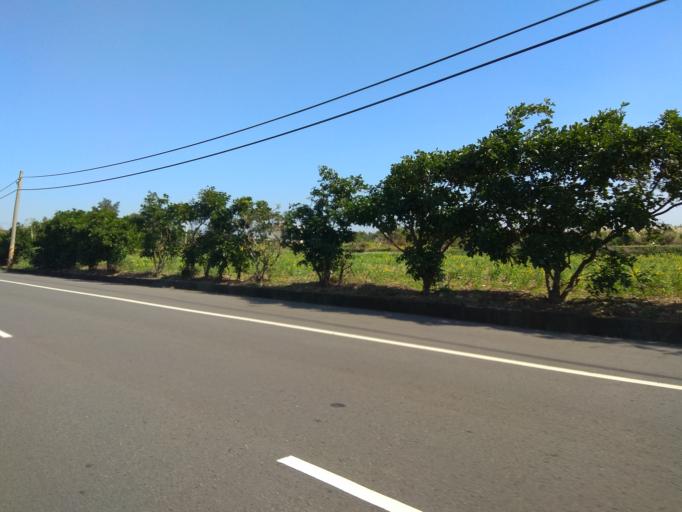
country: TW
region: Taiwan
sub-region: Hsinchu
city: Zhubei
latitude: 25.0195
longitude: 121.0553
